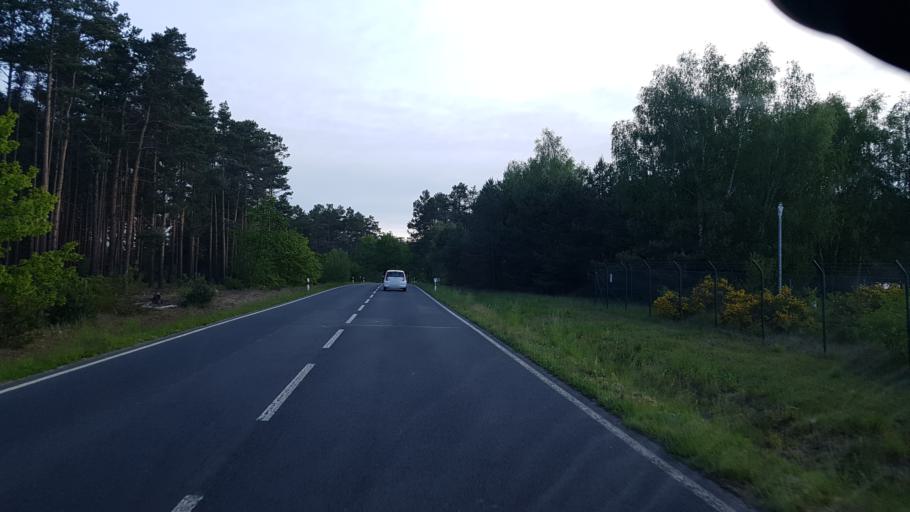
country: DE
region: Brandenburg
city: Sonnewalde
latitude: 51.7320
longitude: 13.6788
